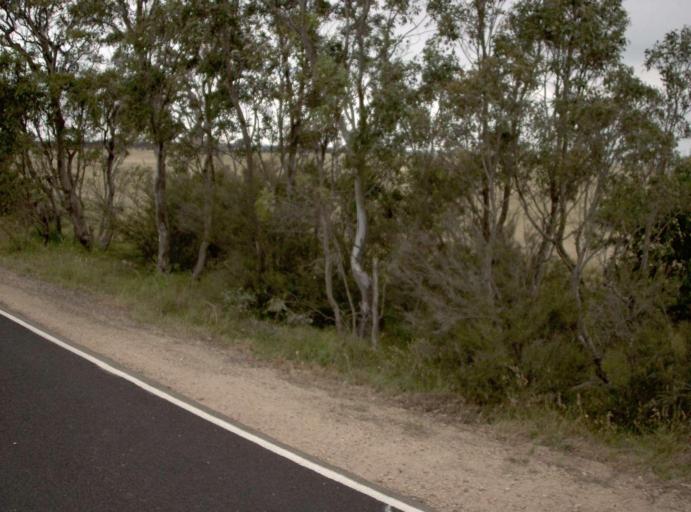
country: AU
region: Victoria
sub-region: Wellington
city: Sale
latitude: -37.9962
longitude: 147.2087
